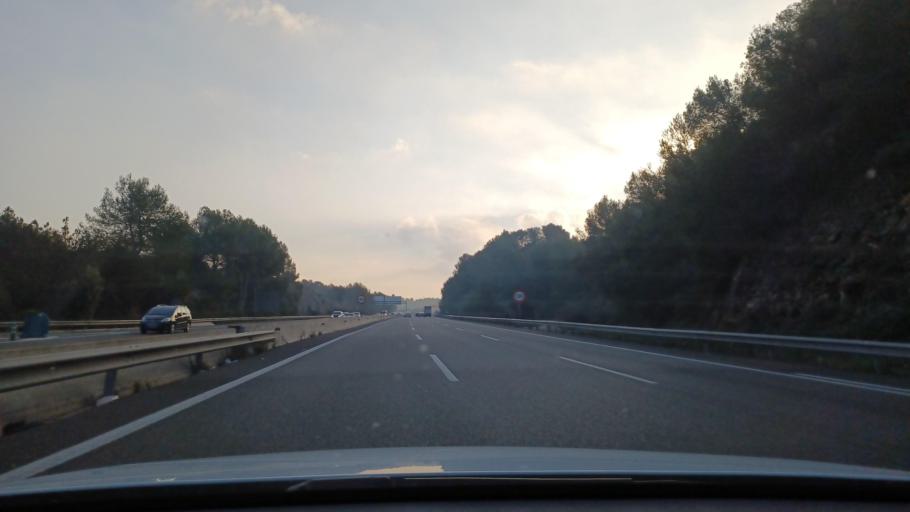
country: ES
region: Catalonia
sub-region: Provincia de Tarragona
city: Tarragona
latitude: 41.1440
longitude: 1.2424
